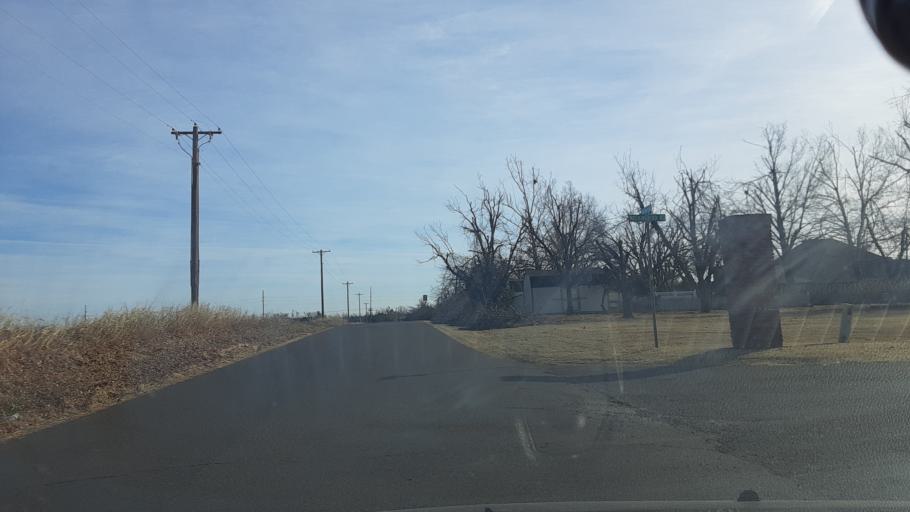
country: US
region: Oklahoma
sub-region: Logan County
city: Guthrie
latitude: 35.8924
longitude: -97.4114
